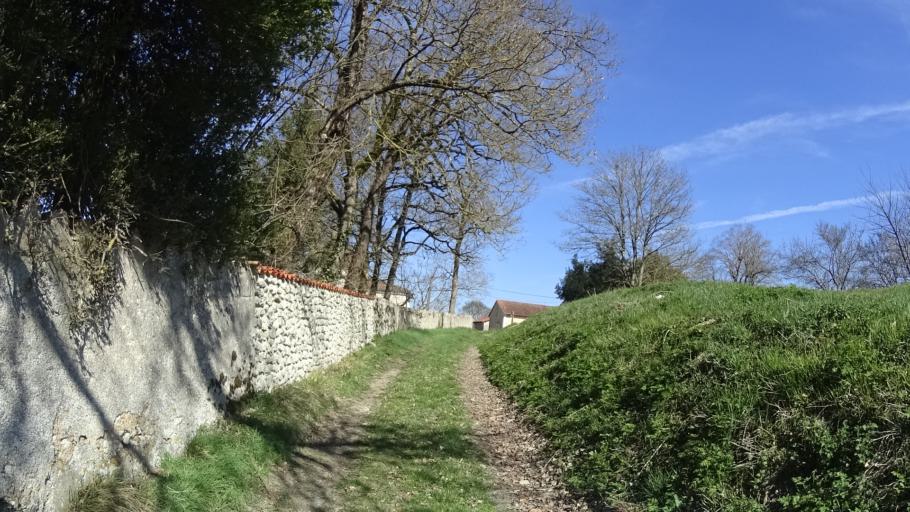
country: FR
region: Aquitaine
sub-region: Departement de la Dordogne
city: Riberac
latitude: 45.2302
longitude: 0.3342
